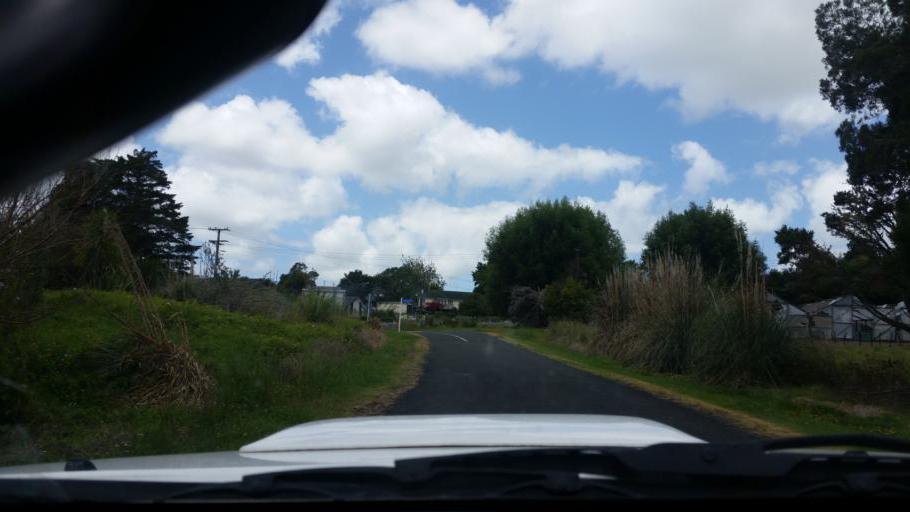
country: NZ
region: Northland
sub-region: Whangarei
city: Ruakaka
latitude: -36.0994
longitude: 174.2418
